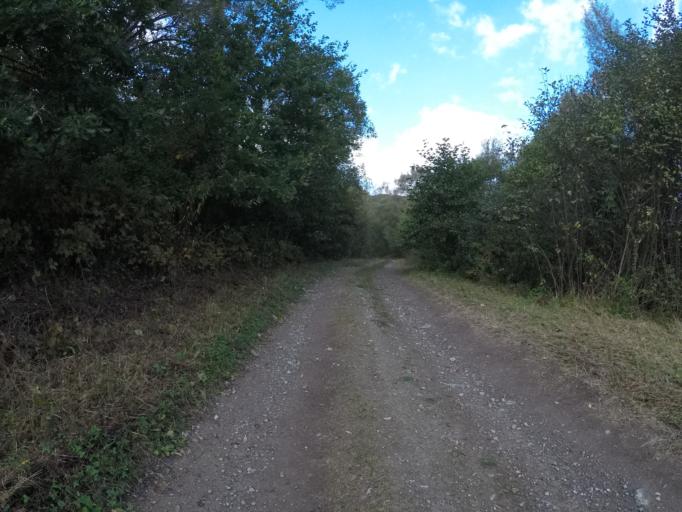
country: SK
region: Presovsky
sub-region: Okres Presov
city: Presov
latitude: 48.9285
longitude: 21.1813
